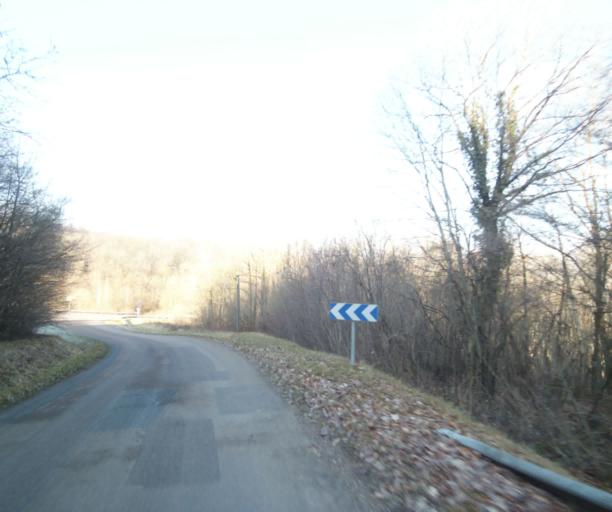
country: FR
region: Champagne-Ardenne
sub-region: Departement de la Haute-Marne
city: Chevillon
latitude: 48.5228
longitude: 5.0910
